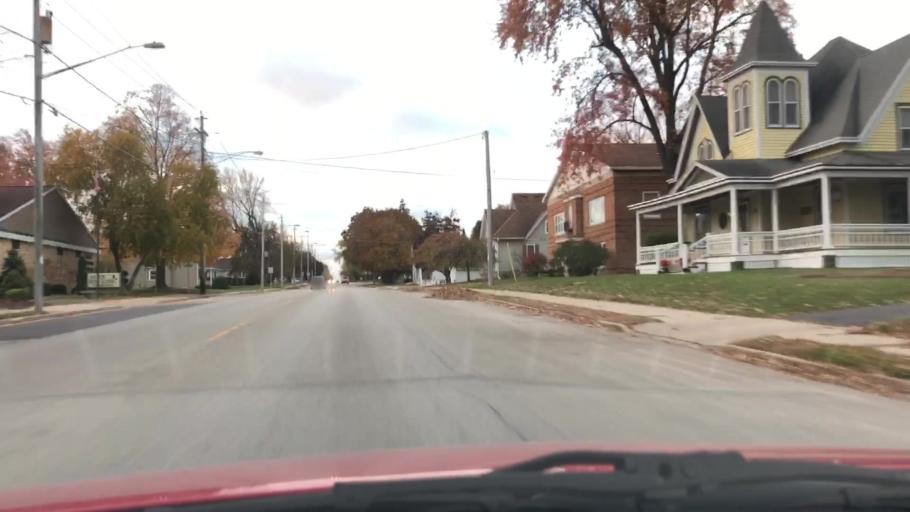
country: US
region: Wisconsin
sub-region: Outagamie County
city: Seymour
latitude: 44.5099
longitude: -88.3304
